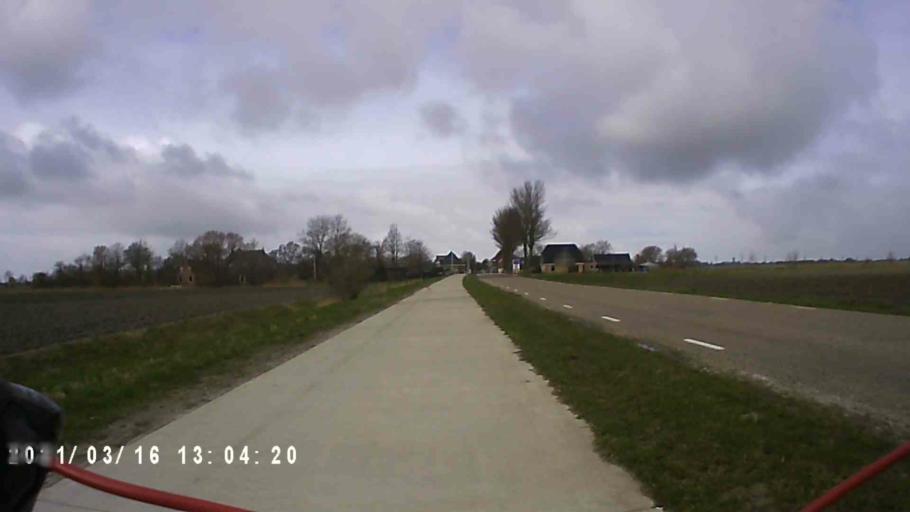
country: NL
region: Friesland
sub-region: Menameradiel
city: Berltsum
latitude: 53.2506
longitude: 5.6321
